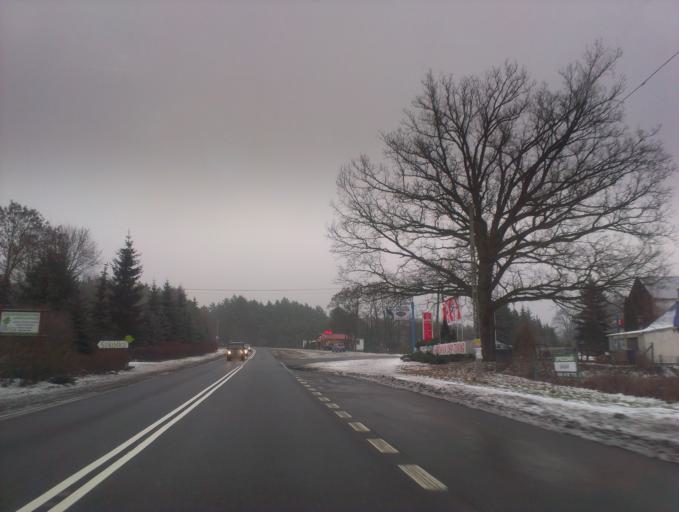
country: PL
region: Greater Poland Voivodeship
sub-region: Powiat pilski
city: Pila
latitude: 53.2204
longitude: 16.7874
